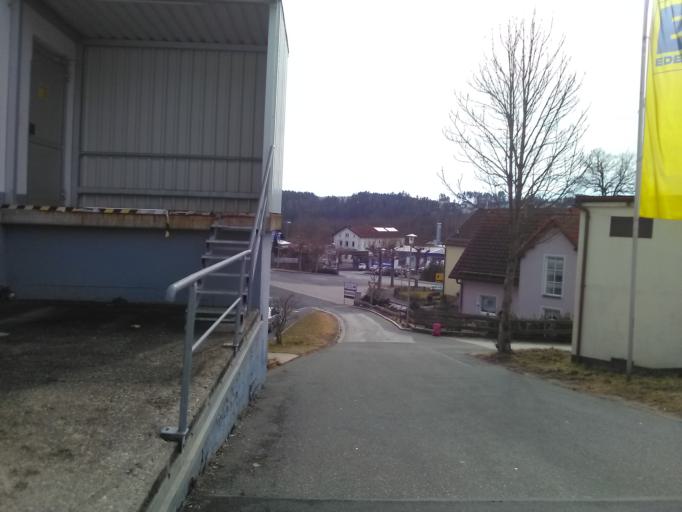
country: DE
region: Bavaria
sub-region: Regierungsbezirk Mittelfranken
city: Neuhaus an der Pegnitz
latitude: 49.6276
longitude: 11.5493
